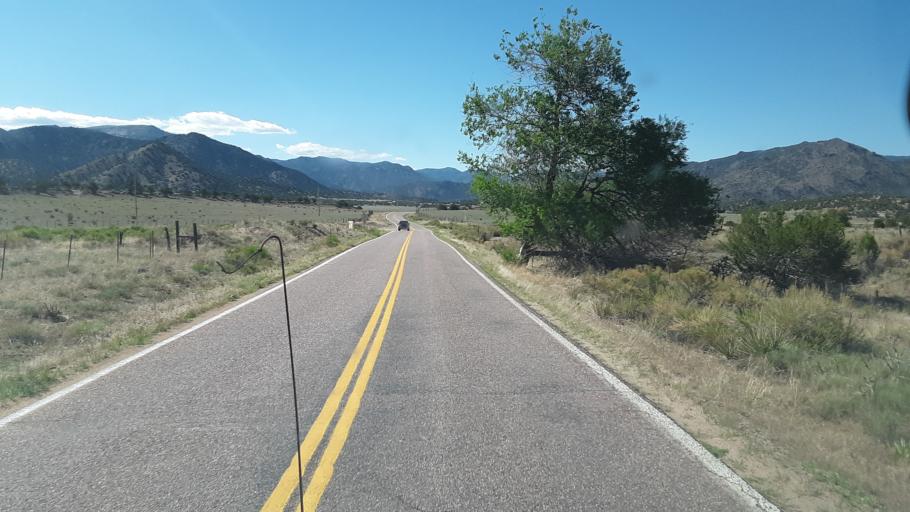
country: US
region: Colorado
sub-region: Fremont County
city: Canon City
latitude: 38.4552
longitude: -105.3732
